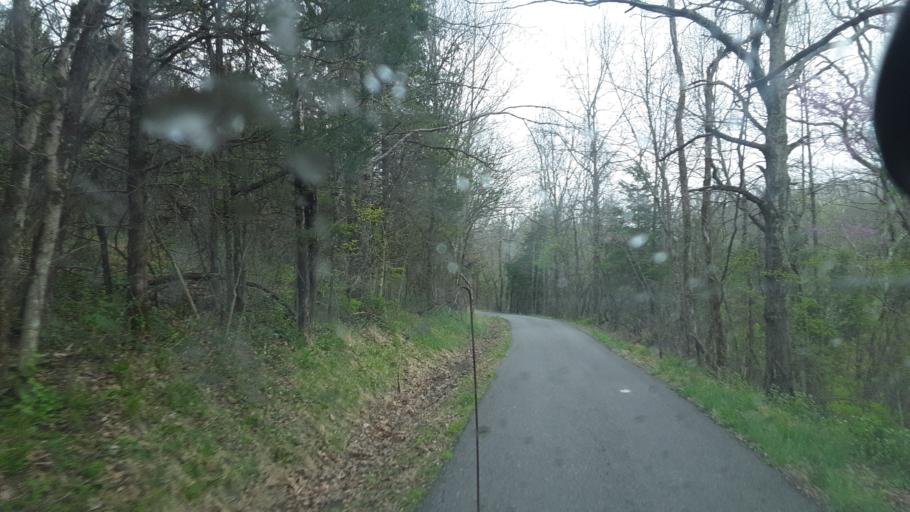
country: US
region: Kentucky
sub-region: Owen County
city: Owenton
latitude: 38.6473
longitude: -84.7887
